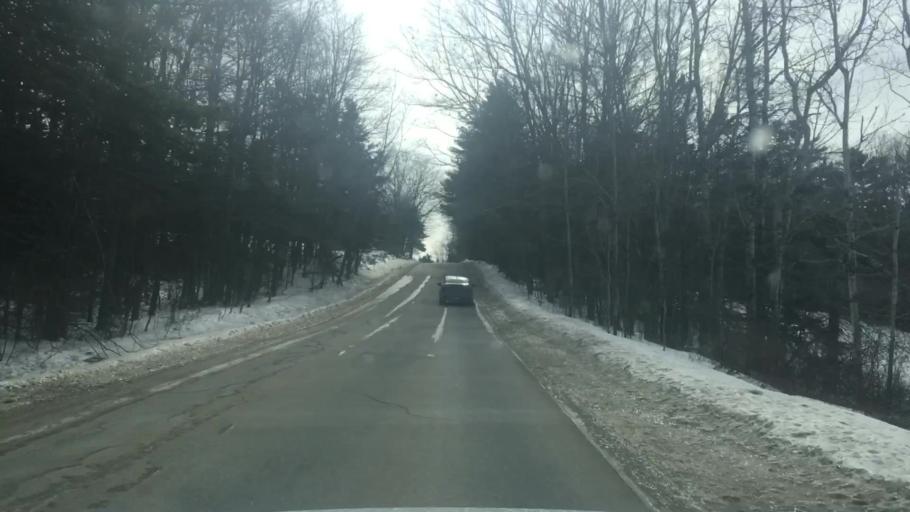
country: US
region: Maine
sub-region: Hancock County
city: Orland
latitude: 44.5900
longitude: -68.7255
